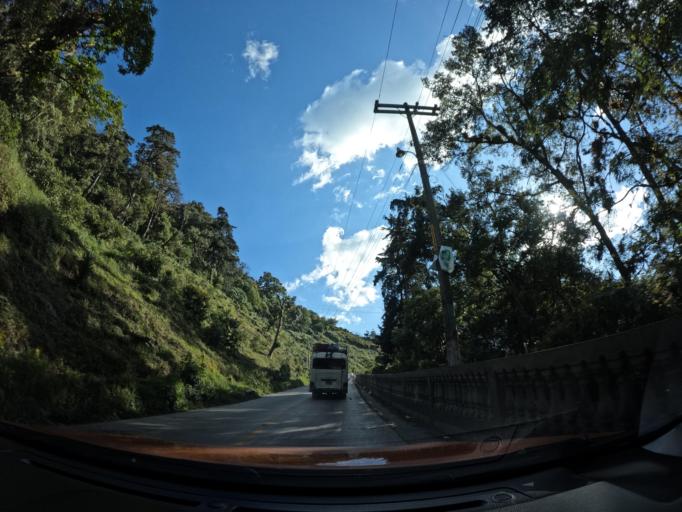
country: GT
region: Sacatepequez
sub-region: Municipio de Santa Maria de Jesus
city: Santa Maria de Jesus
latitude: 14.5006
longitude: -90.7099
